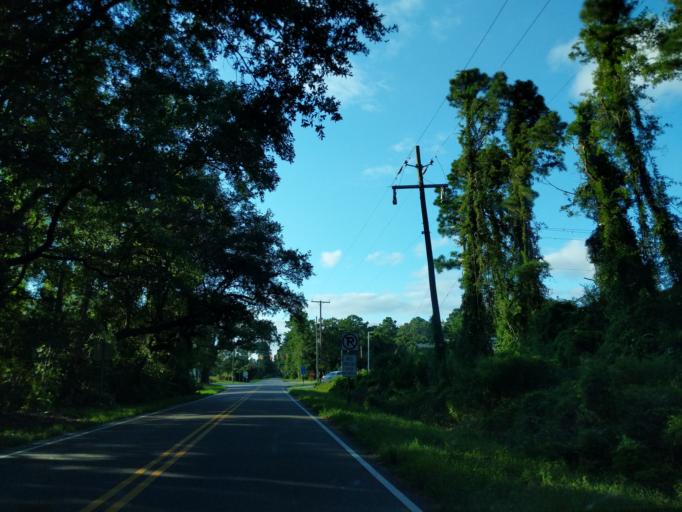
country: US
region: South Carolina
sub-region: Charleston County
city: Awendaw
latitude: 33.0943
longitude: -79.4757
